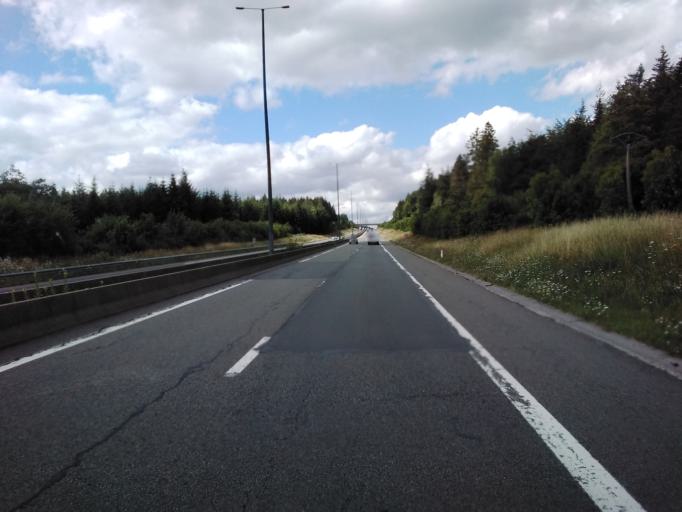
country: BE
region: Wallonia
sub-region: Province de Liege
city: Lierneux
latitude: 50.2101
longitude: 5.7765
